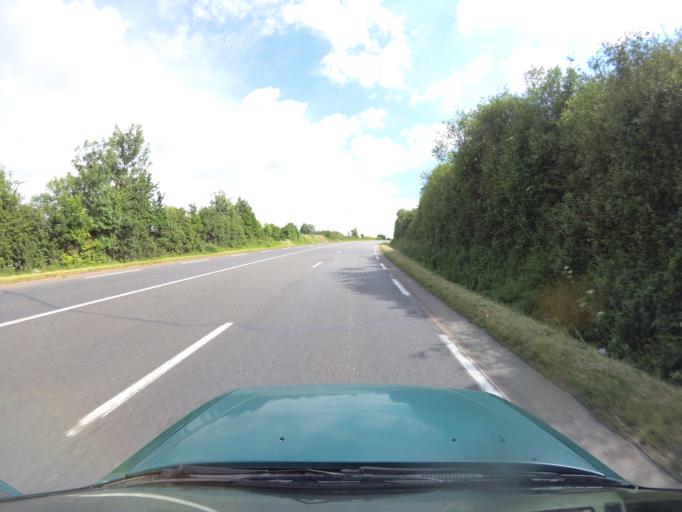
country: FR
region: Pays de la Loire
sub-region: Departement de la Vendee
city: Chantonnay
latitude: 46.6489
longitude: -1.0370
